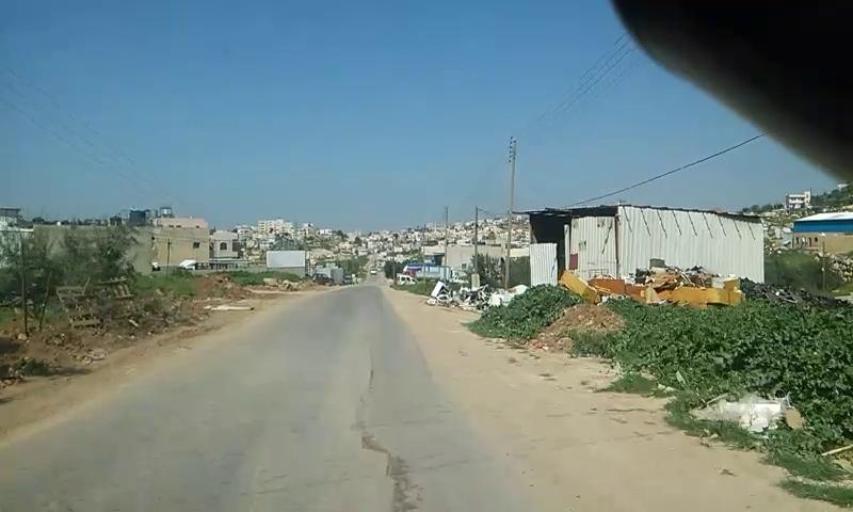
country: PS
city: Dayr Samit
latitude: 31.5106
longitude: 34.9702
